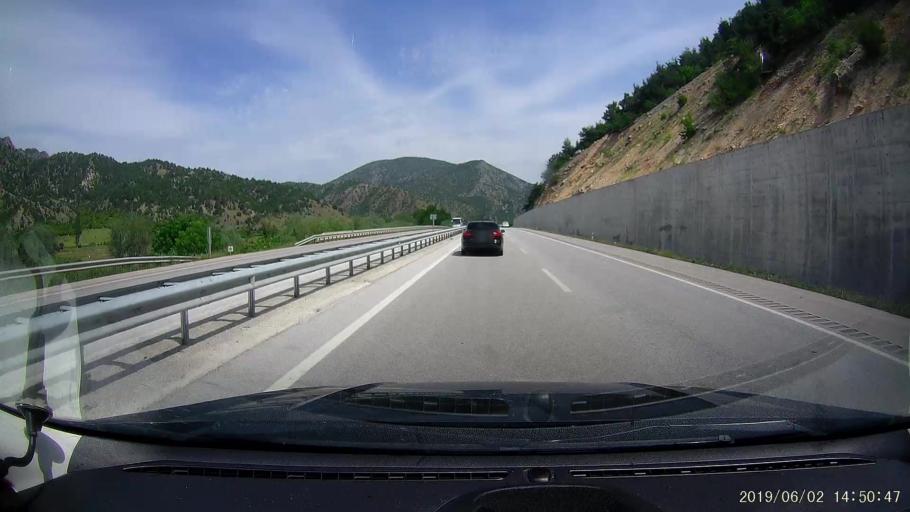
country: TR
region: Corum
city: Kargi
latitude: 41.0694
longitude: 34.5273
